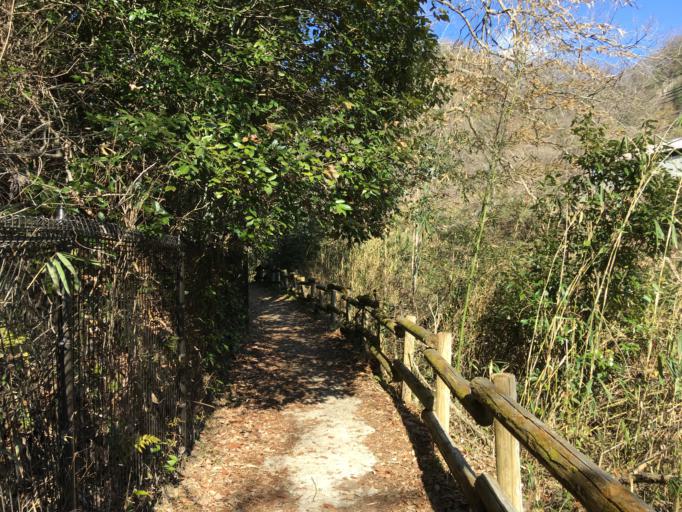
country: JP
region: Osaka
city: Neyagawa
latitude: 34.7601
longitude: 135.6884
